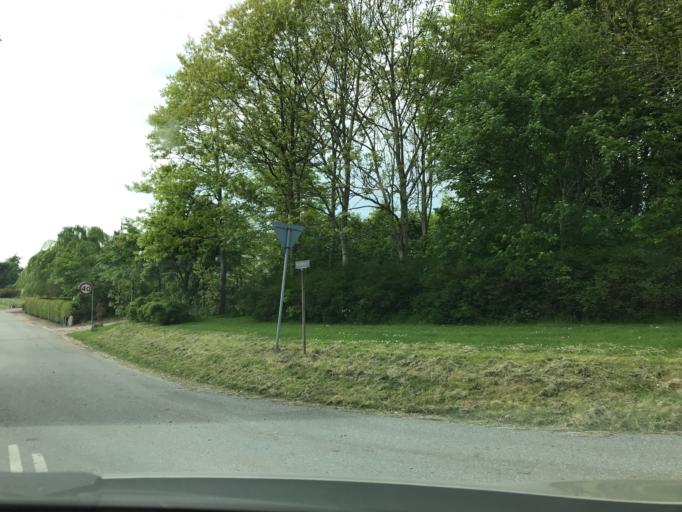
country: DK
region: South Denmark
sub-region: Middelfart Kommune
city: Ejby
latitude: 55.3544
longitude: 9.8994
